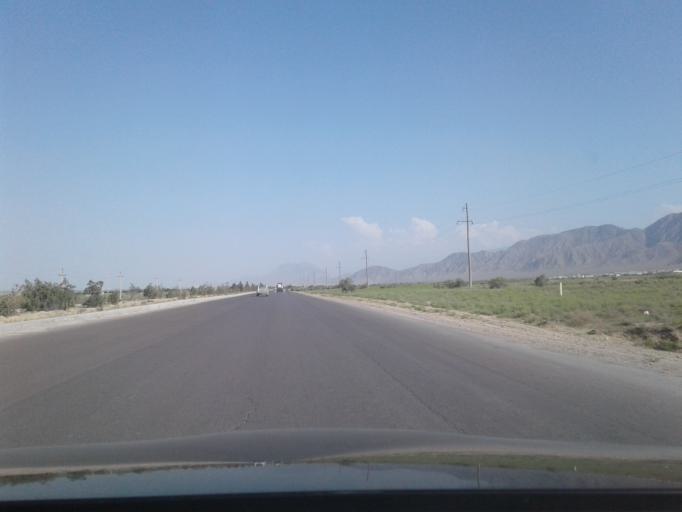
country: TM
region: Ahal
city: Arcabil
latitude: 38.2121
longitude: 57.8114
